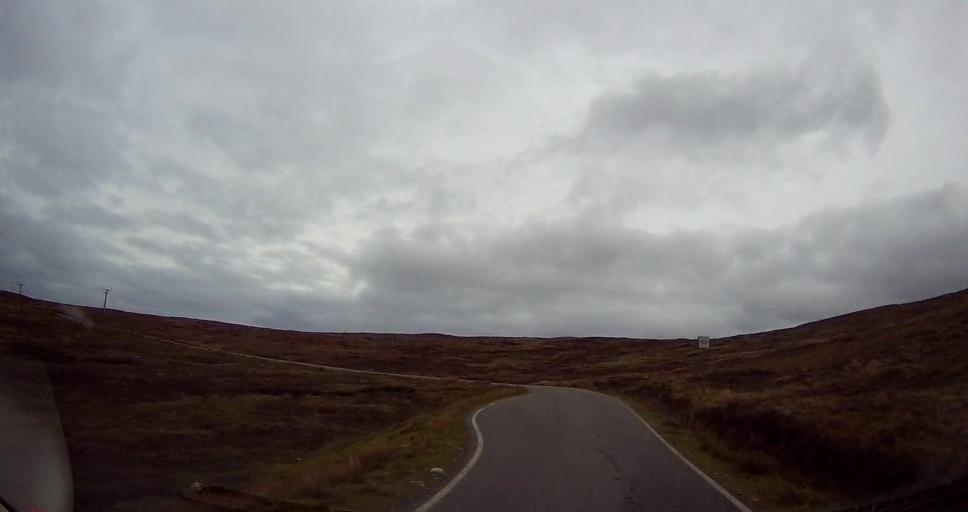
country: GB
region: Scotland
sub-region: Shetland Islands
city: Shetland
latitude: 60.5464
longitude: -1.0603
